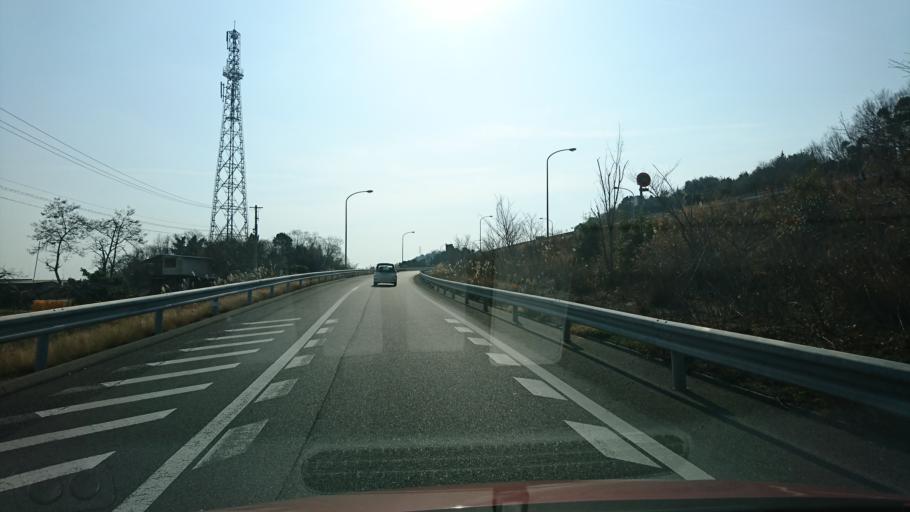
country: JP
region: Hiroshima
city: Onomichi
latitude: 34.4311
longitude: 133.2183
